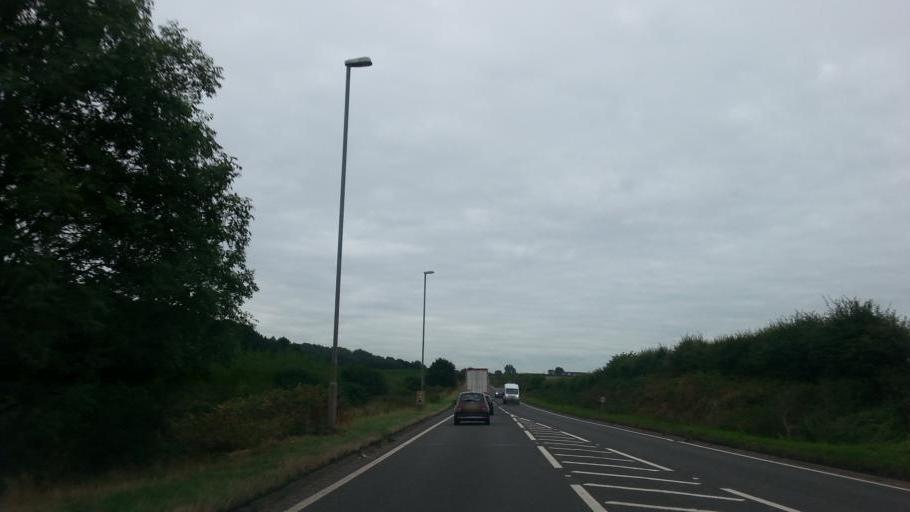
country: GB
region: England
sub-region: Nottinghamshire
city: Bilsthorpe
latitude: 53.1300
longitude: -1.0545
